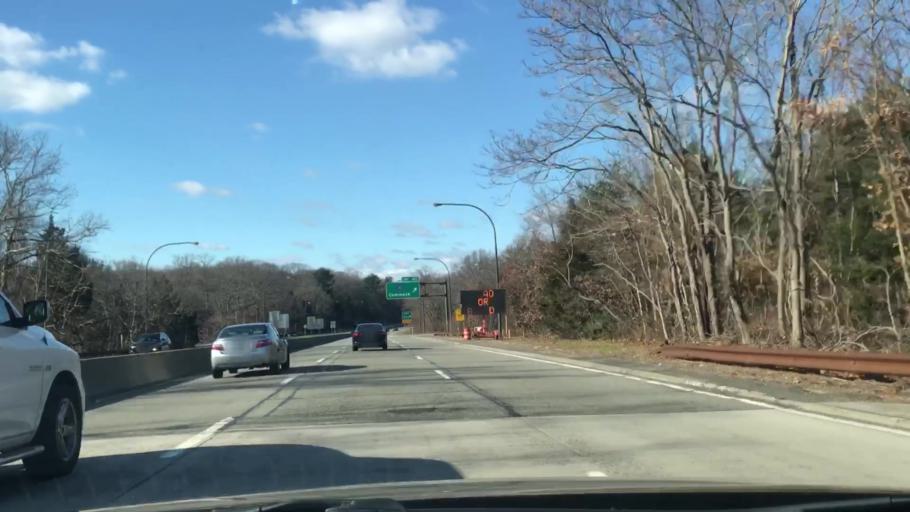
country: US
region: New York
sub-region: Suffolk County
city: Commack
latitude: 40.8186
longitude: -73.2938
